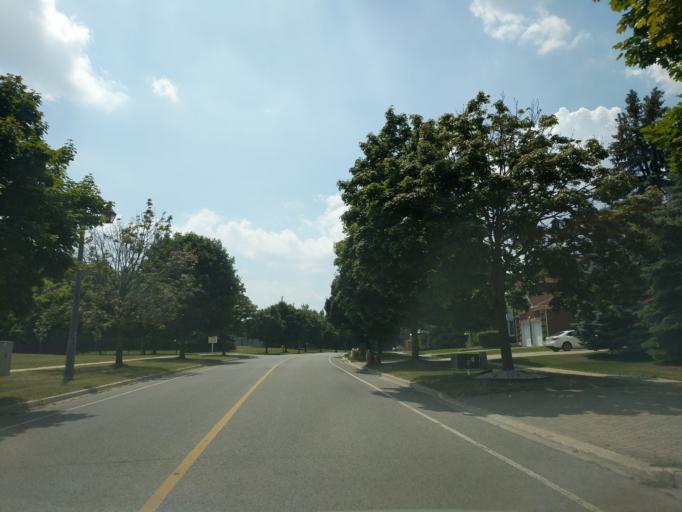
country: CA
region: Ontario
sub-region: York
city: Richmond Hill
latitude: 43.8710
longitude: -79.4025
